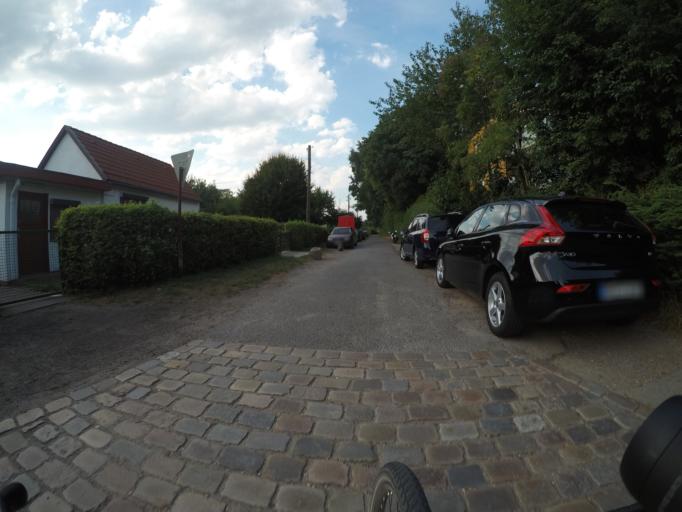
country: DE
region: Hamburg
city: Wandsbek
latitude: 53.5620
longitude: 10.1013
